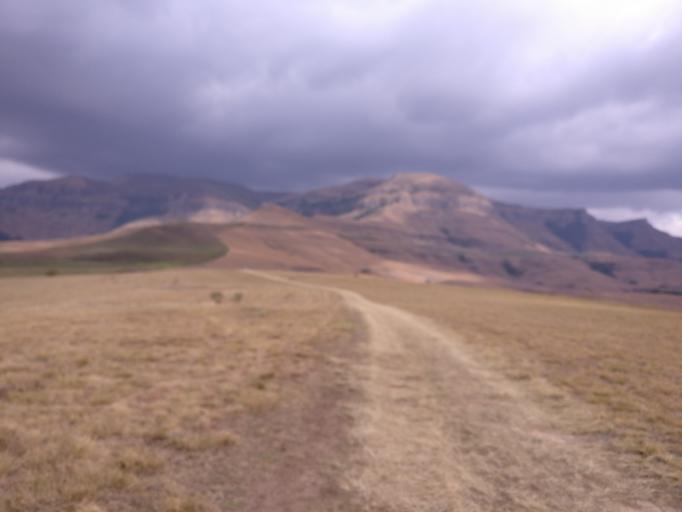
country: ZA
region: KwaZulu-Natal
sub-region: uThukela District Municipality
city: Bergville
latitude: -29.0162
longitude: 29.4149
